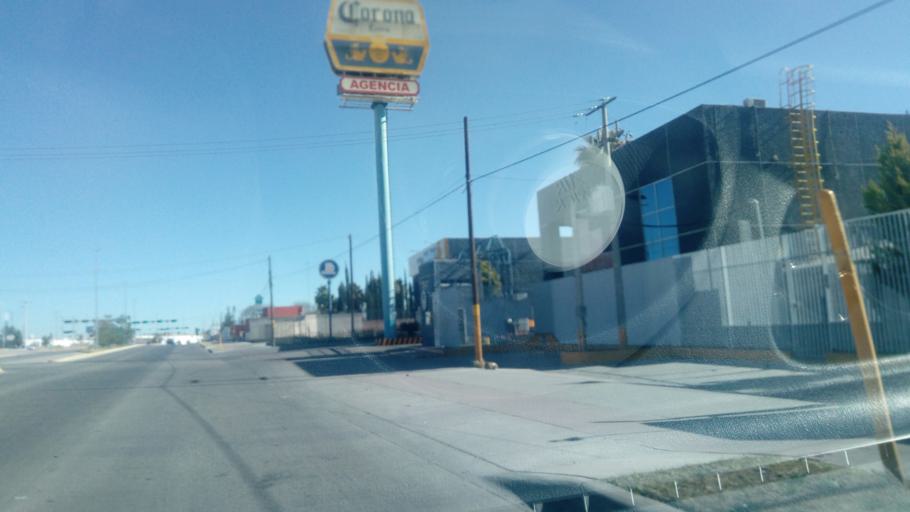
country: MX
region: Durango
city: Victoria de Durango
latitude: 24.0889
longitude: -104.5805
